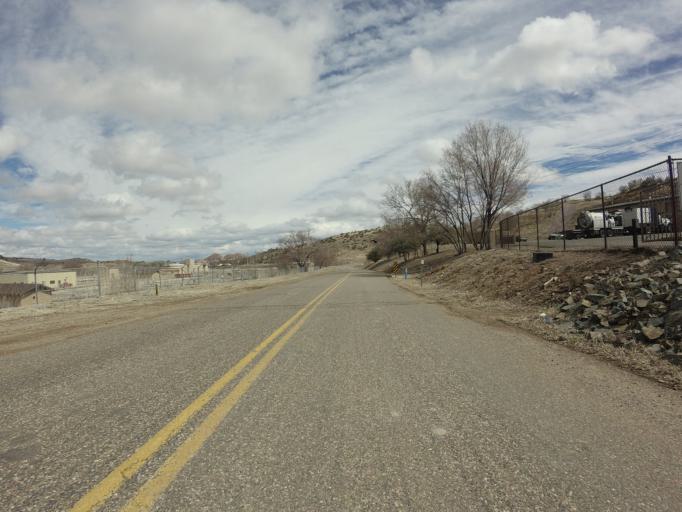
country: US
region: Arizona
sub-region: Yavapai County
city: Prescott
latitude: 34.5700
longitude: -112.4322
